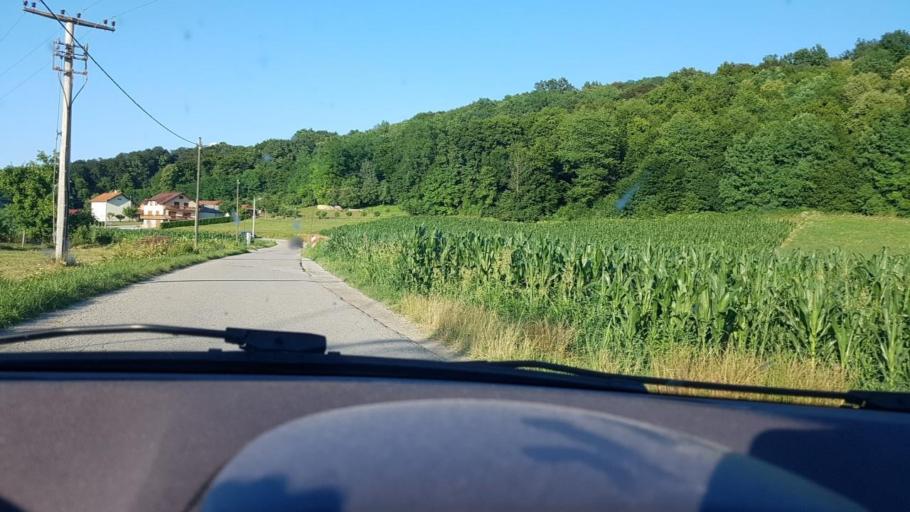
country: HR
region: Krapinsko-Zagorska
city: Zabok
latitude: 46.0800
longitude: 15.9292
